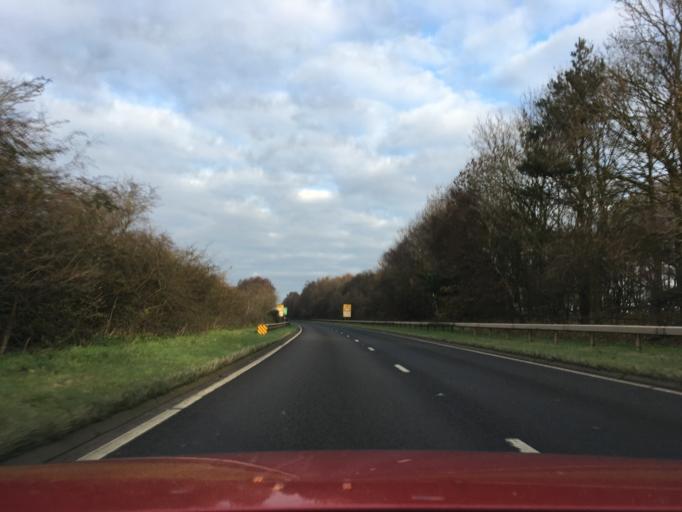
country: GB
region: England
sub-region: Staffordshire
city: Shenstone
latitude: 52.6105
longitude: -1.7958
